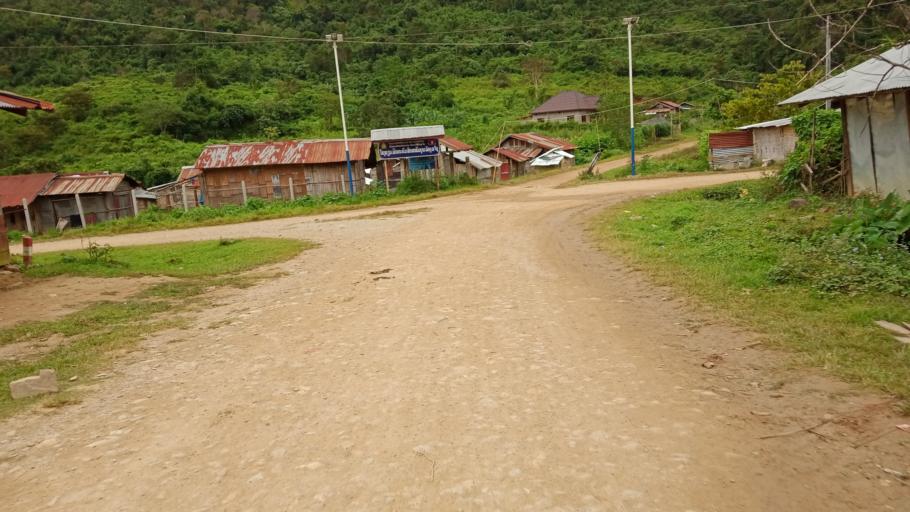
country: LA
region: Xiangkhoang
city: Phonsavan
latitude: 19.1135
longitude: 102.9145
